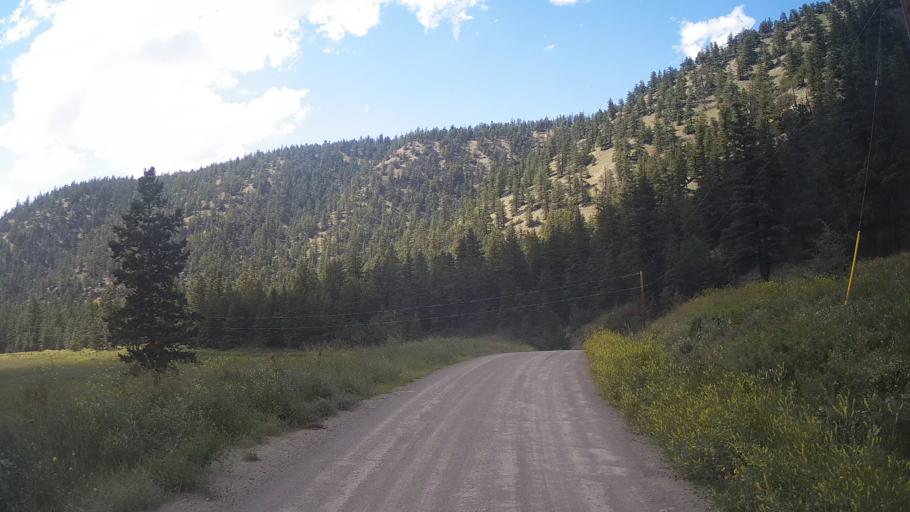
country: CA
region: British Columbia
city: Lillooet
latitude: 51.2517
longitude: -122.0188
